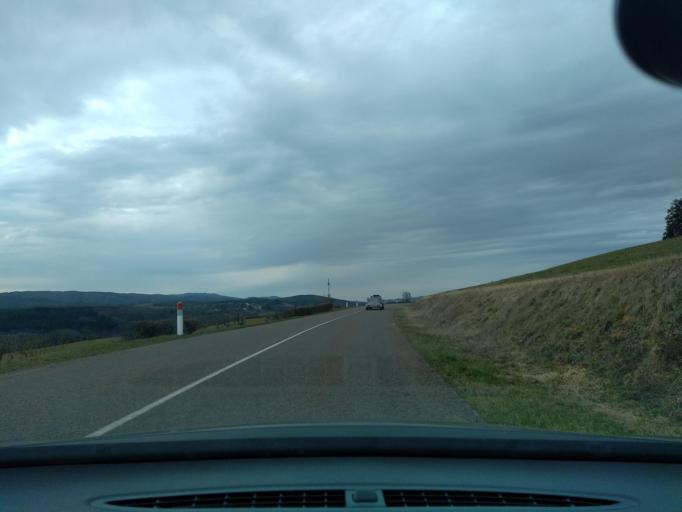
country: FR
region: Franche-Comte
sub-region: Departement du Jura
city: Orgelet
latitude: 46.5117
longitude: 5.6066
